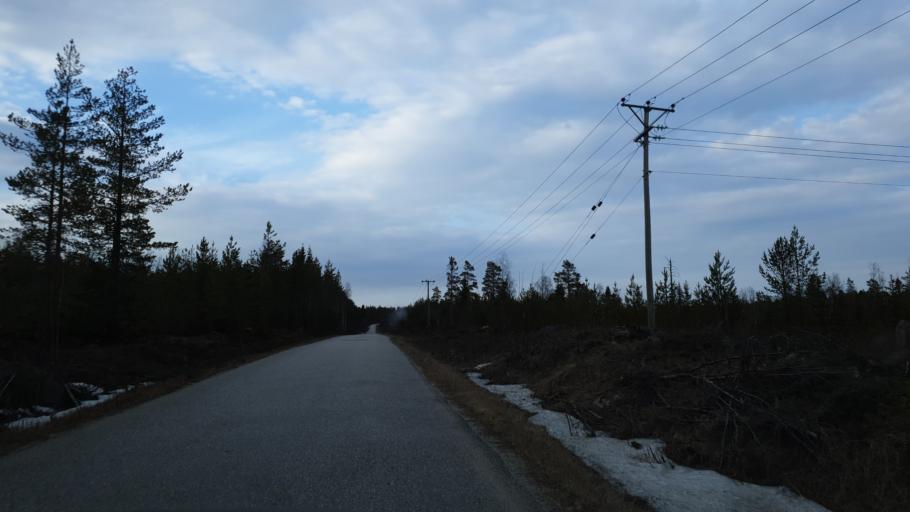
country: SE
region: Vaesternorrland
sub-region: Sundsvalls Kommun
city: Njurundabommen
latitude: 61.9996
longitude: 17.3895
